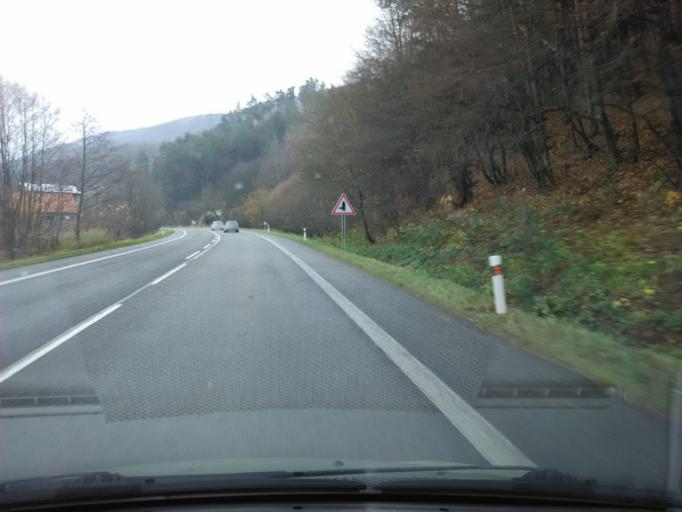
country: SK
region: Banskobystricky
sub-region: Okres Ziar nad Hronom
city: Kremnica
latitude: 48.6795
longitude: 18.9167
